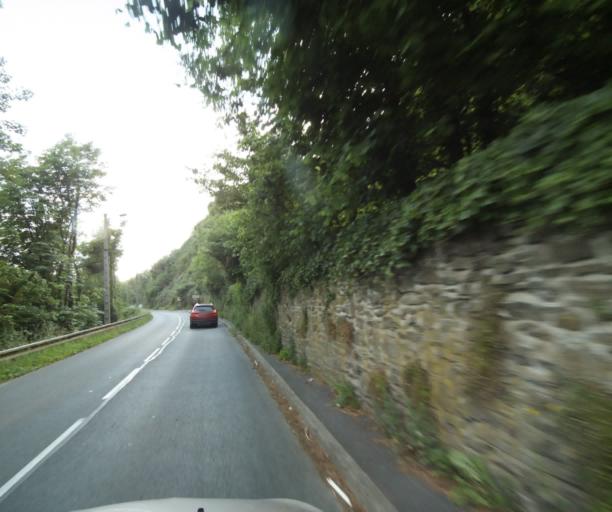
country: FR
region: Champagne-Ardenne
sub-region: Departement des Ardennes
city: Charleville-Mezieres
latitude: 49.7843
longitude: 4.7211
